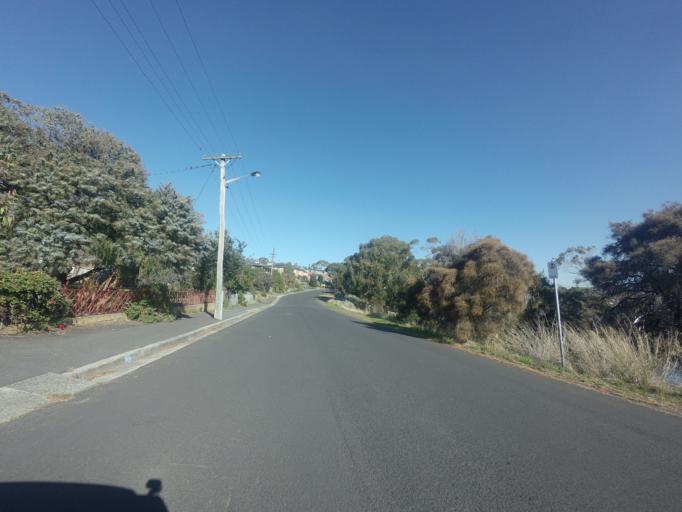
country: AU
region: Tasmania
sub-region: Clarence
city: Bellerive
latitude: -42.8688
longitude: 147.3539
